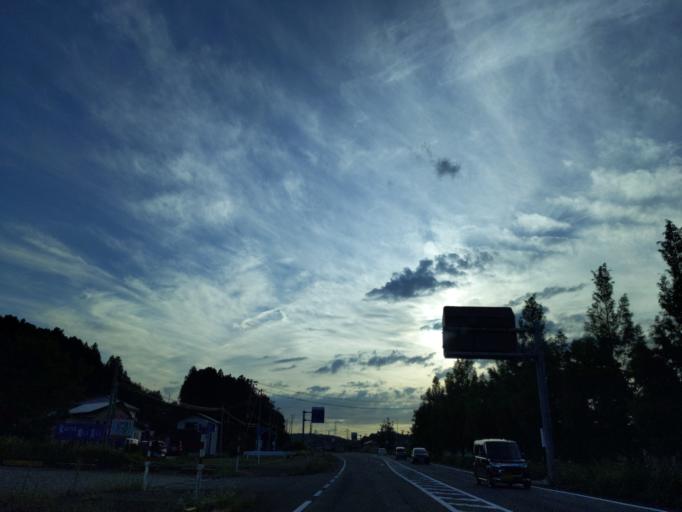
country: JP
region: Niigata
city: Kashiwazaki
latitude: 37.4529
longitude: 138.6531
